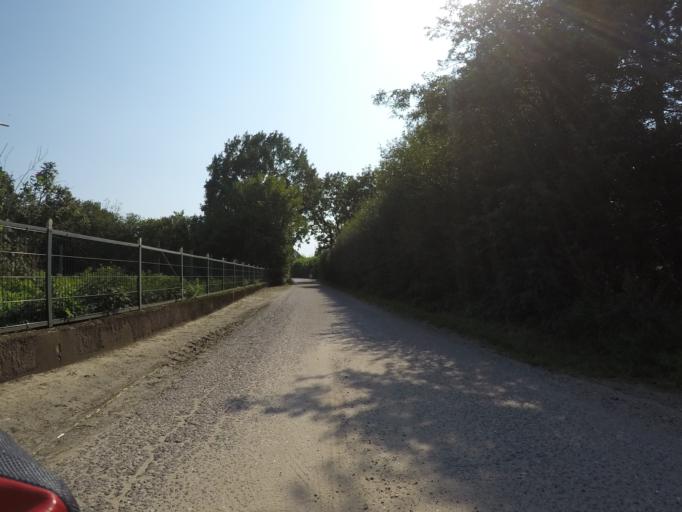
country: DE
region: Schleswig-Holstein
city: Stuvenborn
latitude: 53.8586
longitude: 10.1489
